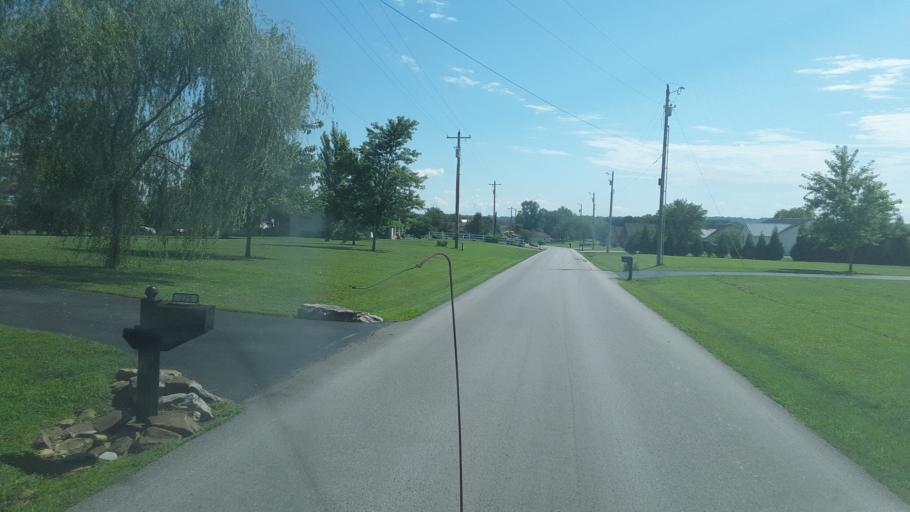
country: US
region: Kentucky
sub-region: Todd County
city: Elkton
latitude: 36.8113
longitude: -87.1801
